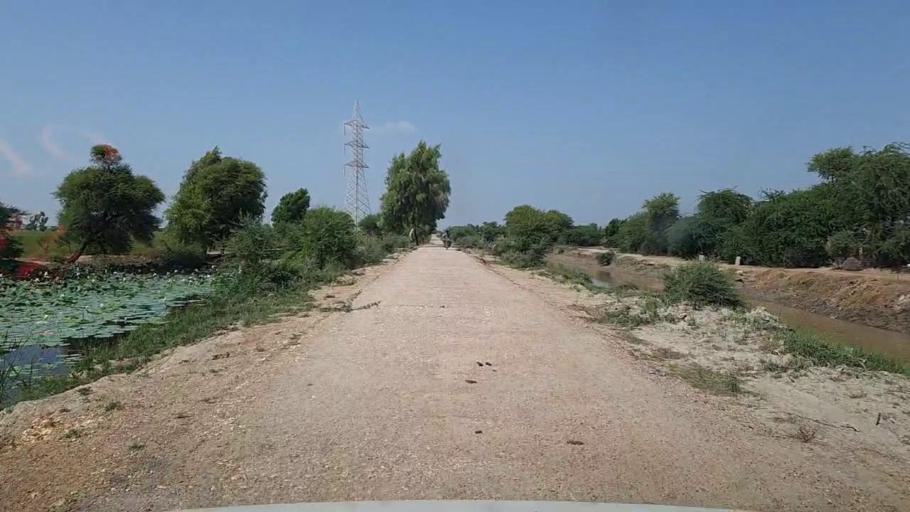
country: PK
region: Sindh
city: Kario
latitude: 24.6570
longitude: 68.5507
